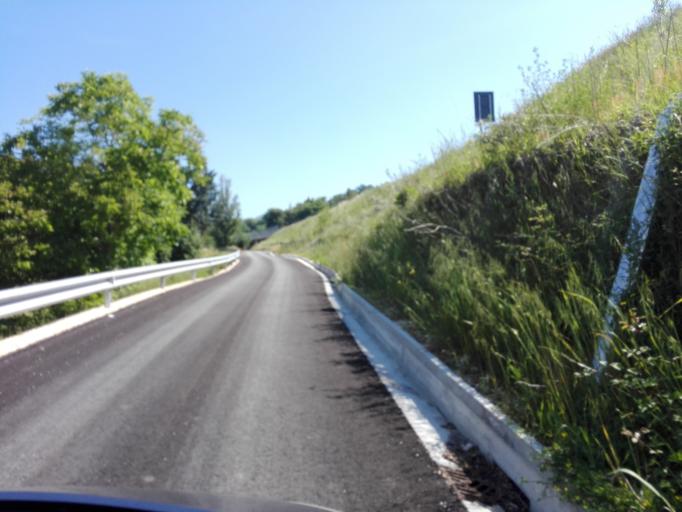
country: IT
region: Umbria
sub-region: Provincia di Perugia
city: Foligno
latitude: 42.9558
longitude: 12.7333
